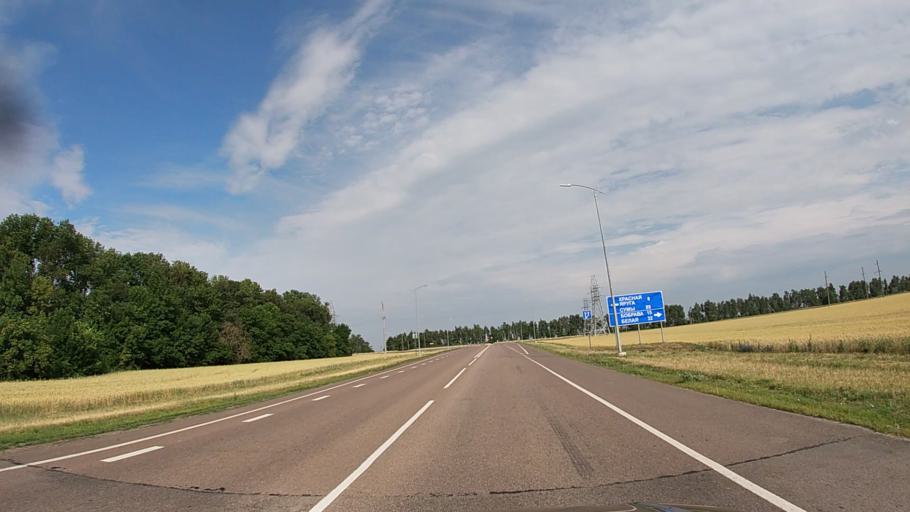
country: RU
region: Belgorod
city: Proletarskiy
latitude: 50.8300
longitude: 35.7700
